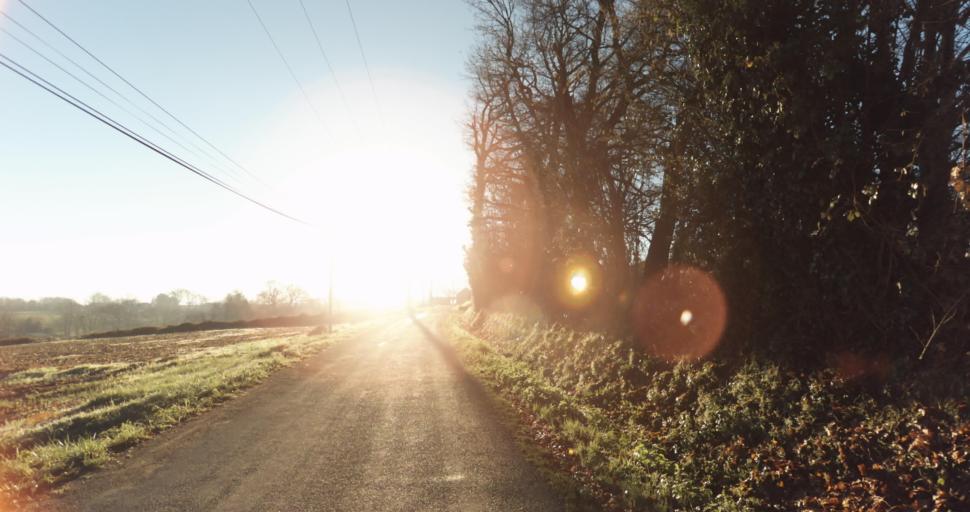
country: FR
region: Aquitaine
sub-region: Departement des Pyrenees-Atlantiques
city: Morlaas
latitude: 43.3322
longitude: -0.2689
